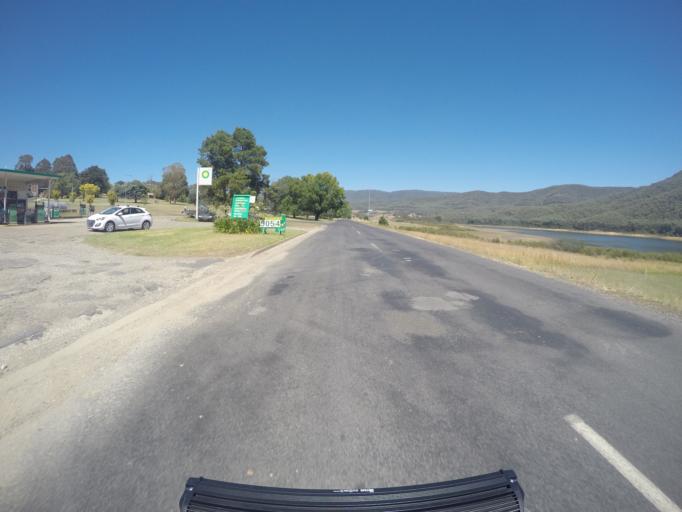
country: AU
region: New South Wales
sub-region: Tumut Shire
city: Tumut
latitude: -35.5809
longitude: 148.2972
